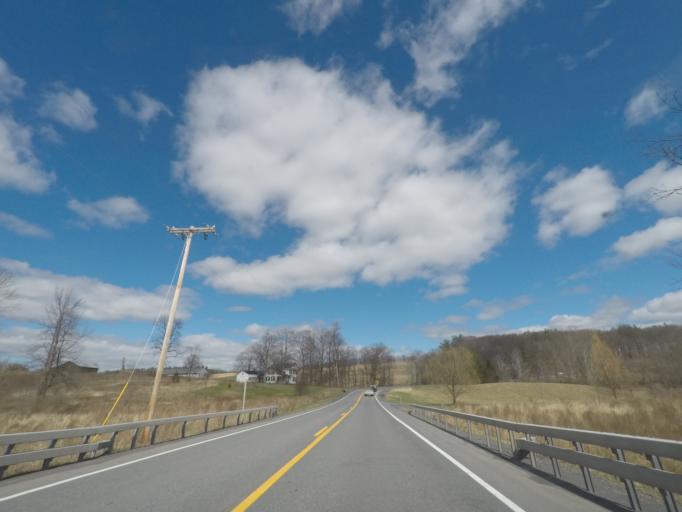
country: US
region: New York
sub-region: Albany County
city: Voorheesville
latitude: 42.5717
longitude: -73.9185
